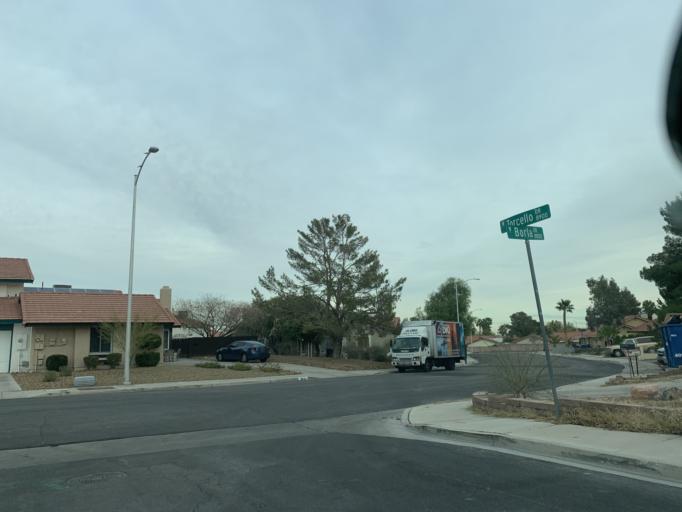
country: US
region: Nevada
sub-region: Clark County
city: Summerlin South
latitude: 36.1562
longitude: -115.2889
